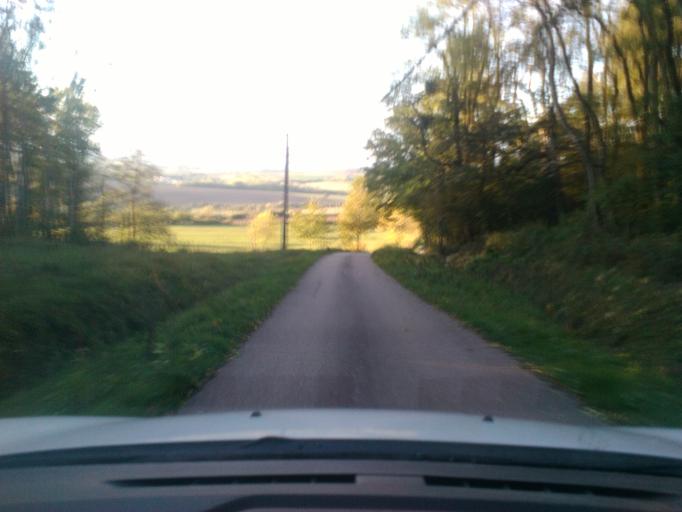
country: FR
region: Lorraine
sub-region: Departement des Vosges
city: Charmes
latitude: 48.3387
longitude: 6.2545
